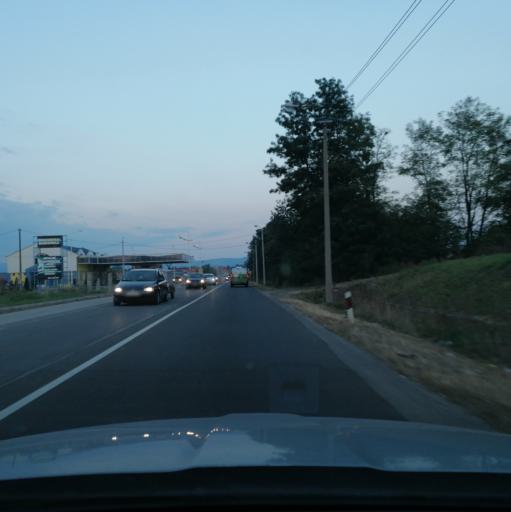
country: RS
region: Central Serbia
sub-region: Raski Okrug
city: Kraljevo
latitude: 43.7025
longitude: 20.7421
